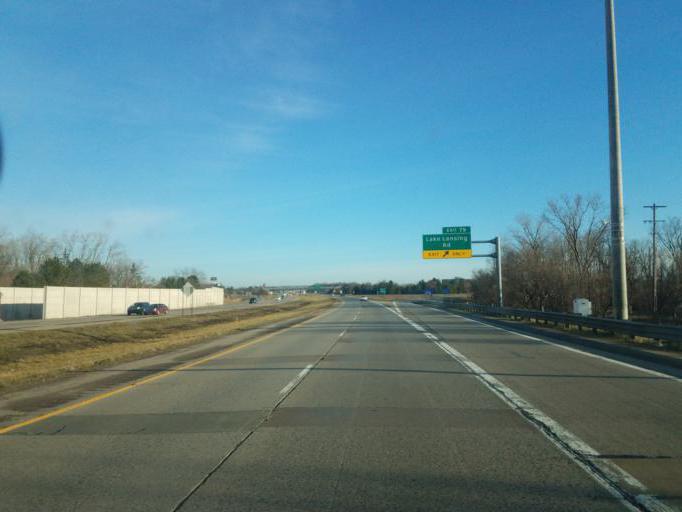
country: US
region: Michigan
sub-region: Ingham County
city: East Lansing
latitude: 42.7554
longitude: -84.5078
